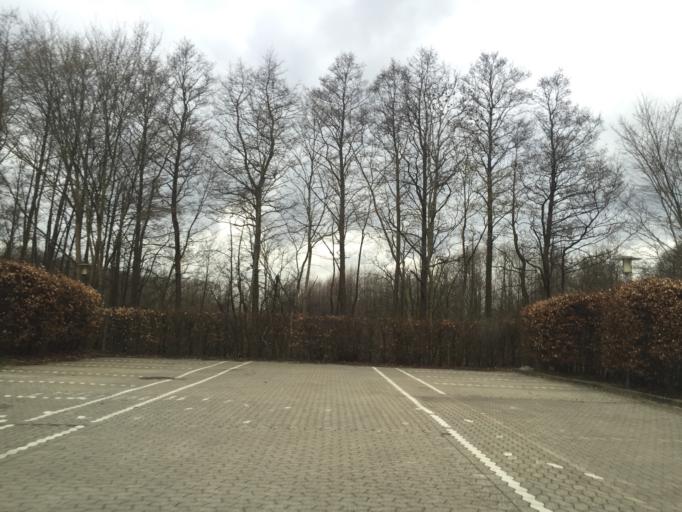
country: DK
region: Capital Region
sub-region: Rudersdal Kommune
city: Holte
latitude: 55.7820
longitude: 12.4464
